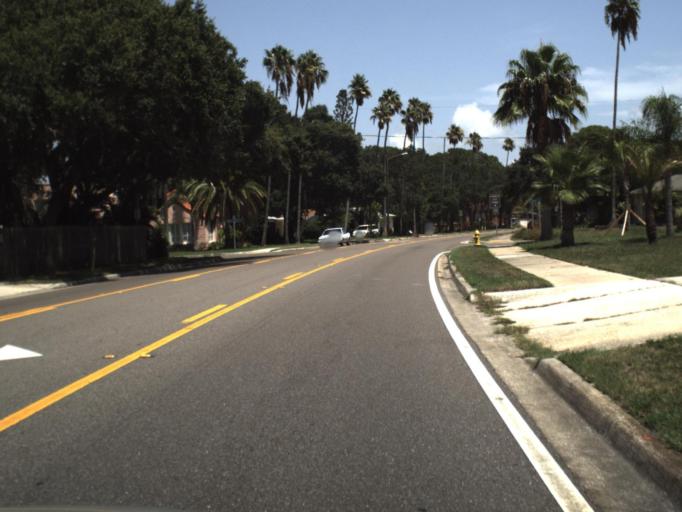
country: US
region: Florida
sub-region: Pinellas County
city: Dunedin
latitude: 28.0323
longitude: -82.7886
